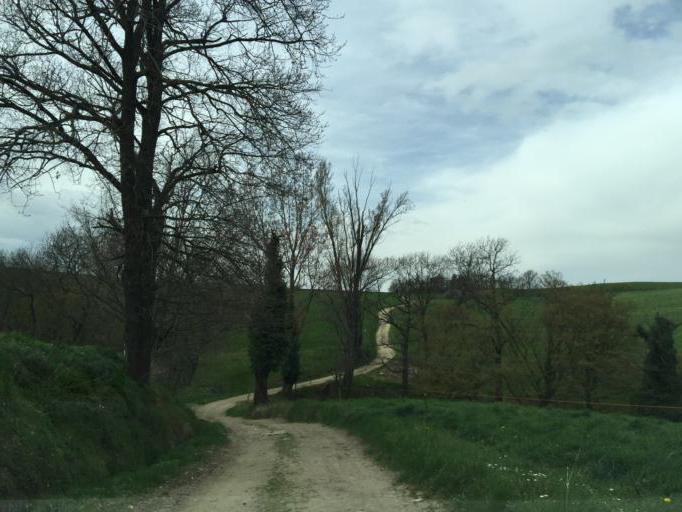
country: FR
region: Rhone-Alpes
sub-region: Departement de la Loire
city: Saint-Paul-en-Jarez
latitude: 45.4774
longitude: 4.5629
